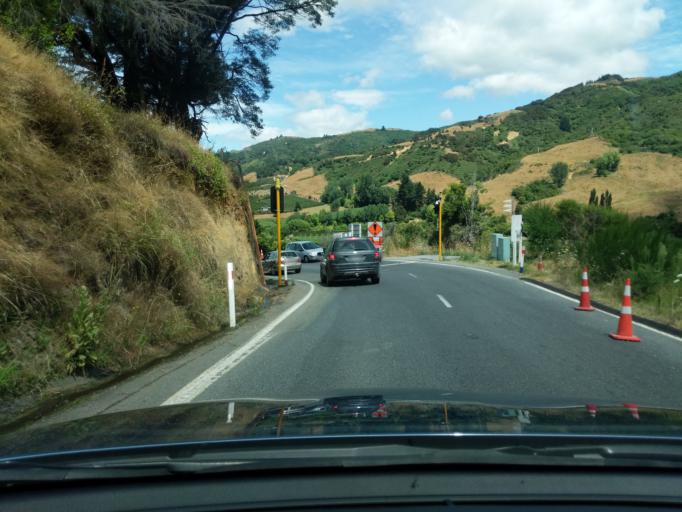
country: NZ
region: Tasman
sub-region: Tasman District
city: Motueka
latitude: -41.0531
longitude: 172.9633
